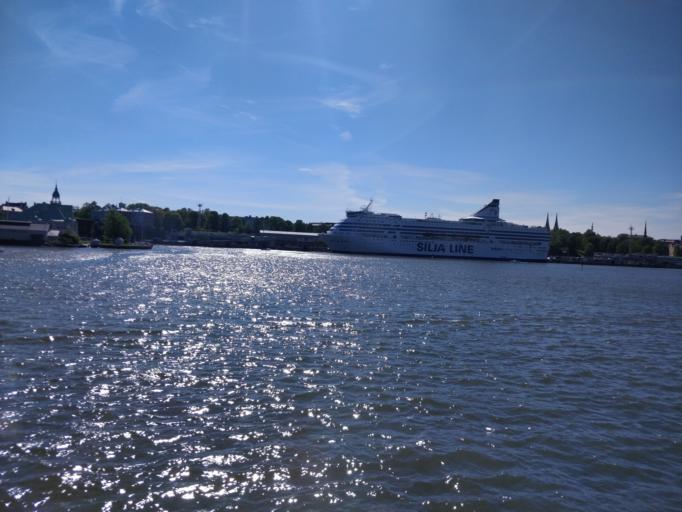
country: FI
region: Uusimaa
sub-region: Helsinki
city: Helsinki
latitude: 60.1632
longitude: 24.9668
